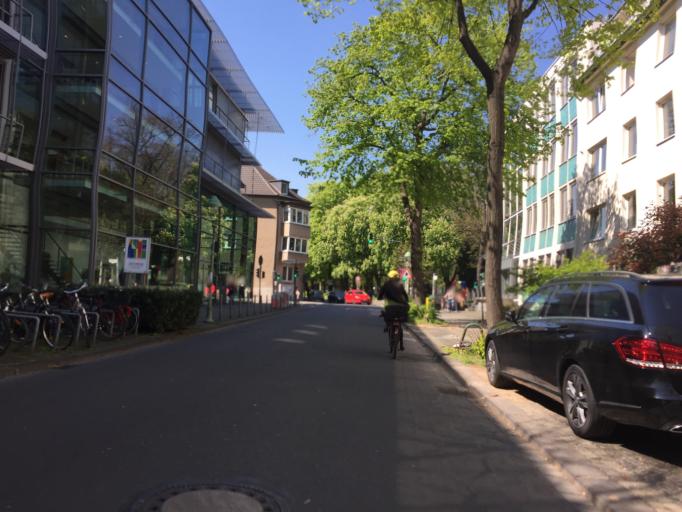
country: DE
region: North Rhine-Westphalia
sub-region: Regierungsbezirk Koln
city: Bonn
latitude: 50.7306
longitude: 7.1052
